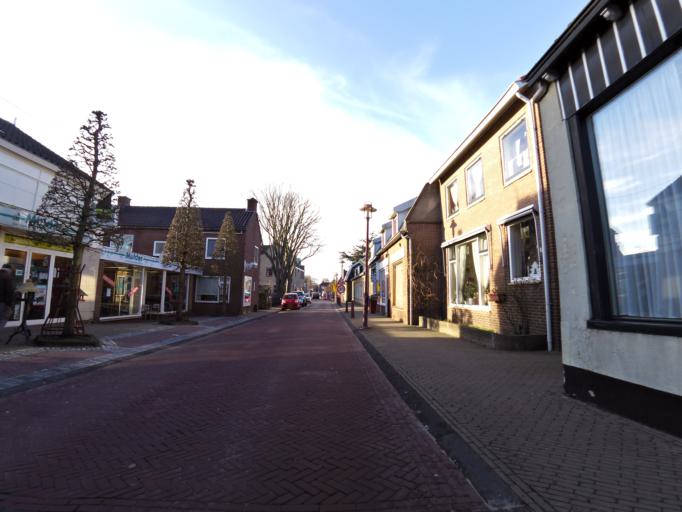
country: NL
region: South Holland
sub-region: Gemeente Hellevoetsluis
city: Nieuw-Helvoet
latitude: 51.8745
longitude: 4.0709
